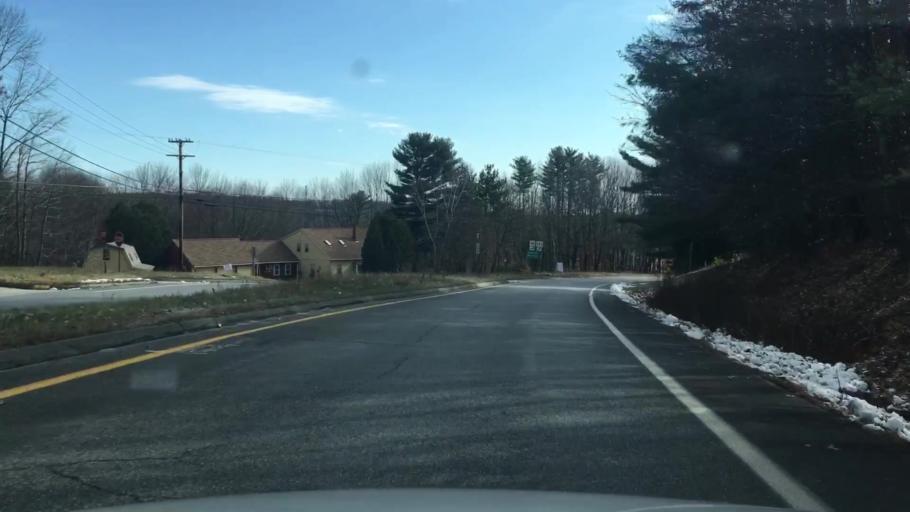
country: US
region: Maine
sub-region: Kennebec County
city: Winthrop
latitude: 44.3216
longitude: -69.9800
